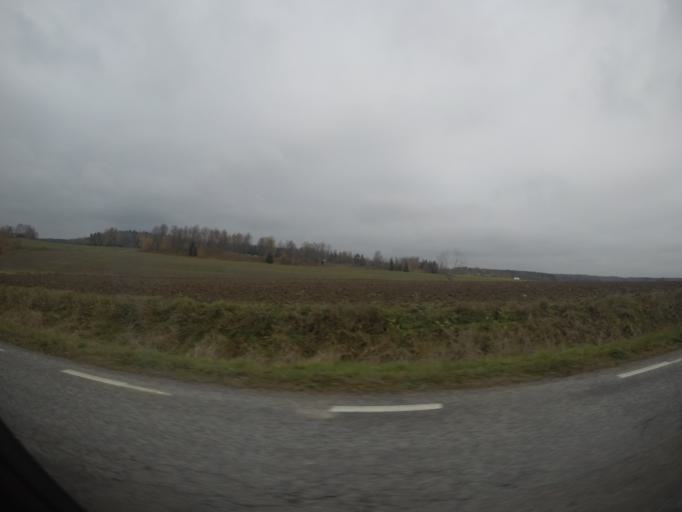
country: SE
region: Vaestmanland
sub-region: Vasteras
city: Skultuna
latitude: 59.6908
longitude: 16.4252
